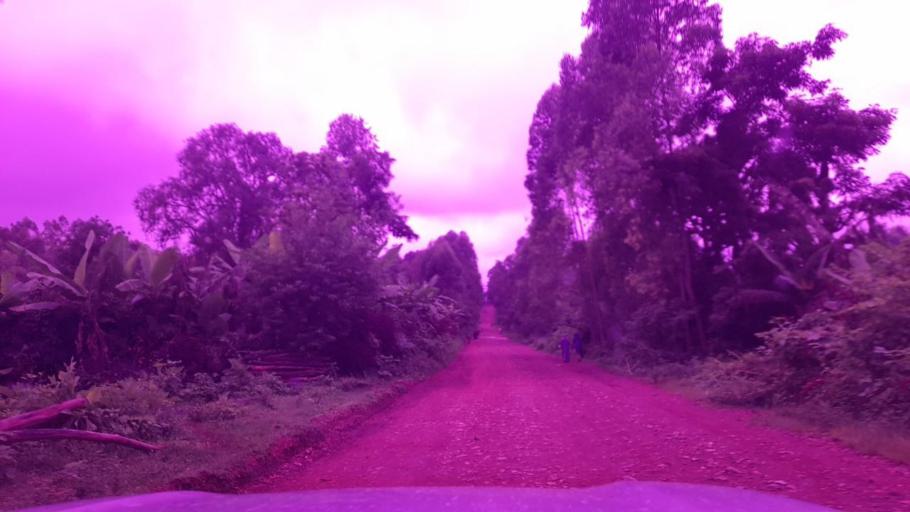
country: ET
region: Southern Nations, Nationalities, and People's Region
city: Bonga
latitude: 7.5807
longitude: 36.0227
